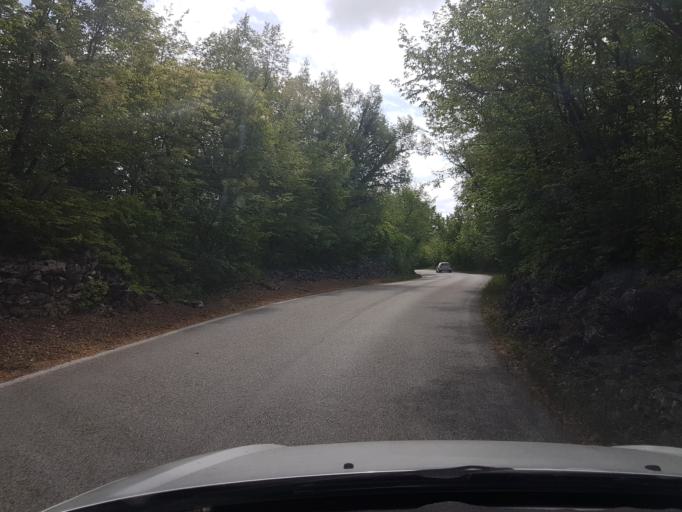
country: IT
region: Friuli Venezia Giulia
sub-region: Provincia di Trieste
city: Aurisina Cave
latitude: 45.7821
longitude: 13.6657
